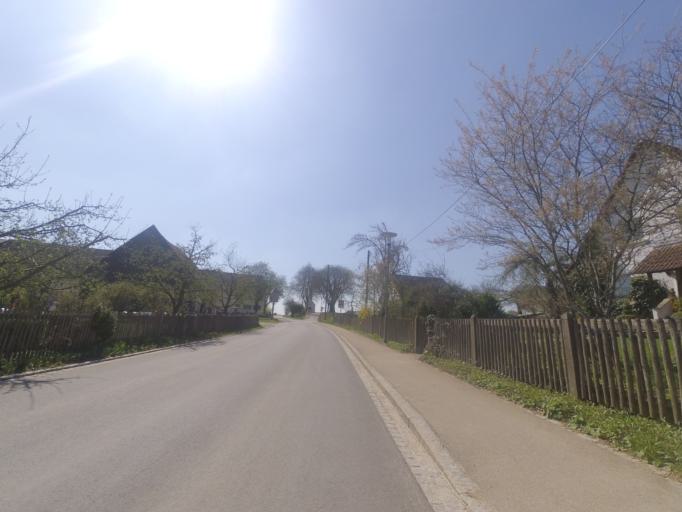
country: DE
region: Bavaria
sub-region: Swabia
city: Roggenburg
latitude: 48.2987
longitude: 10.2119
